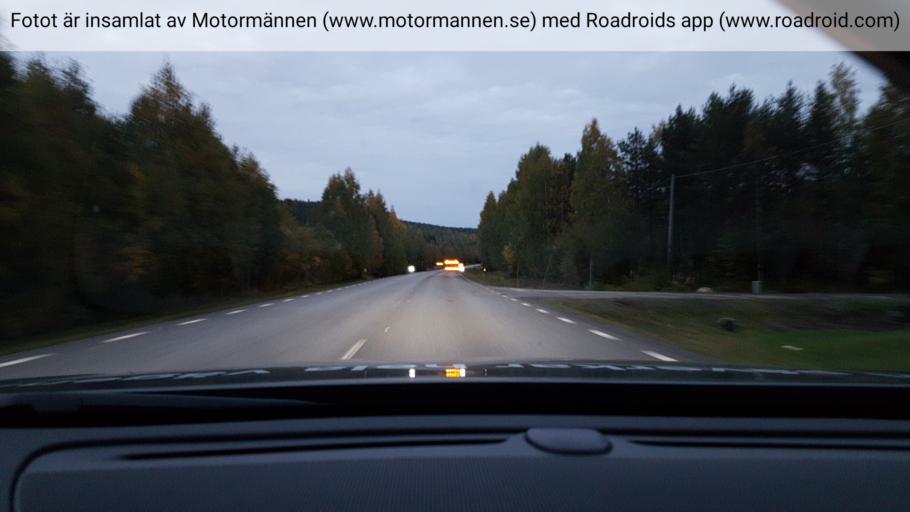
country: SE
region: Norrbotten
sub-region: Alvsbyns Kommun
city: AElvsbyn
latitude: 65.7822
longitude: 20.7985
